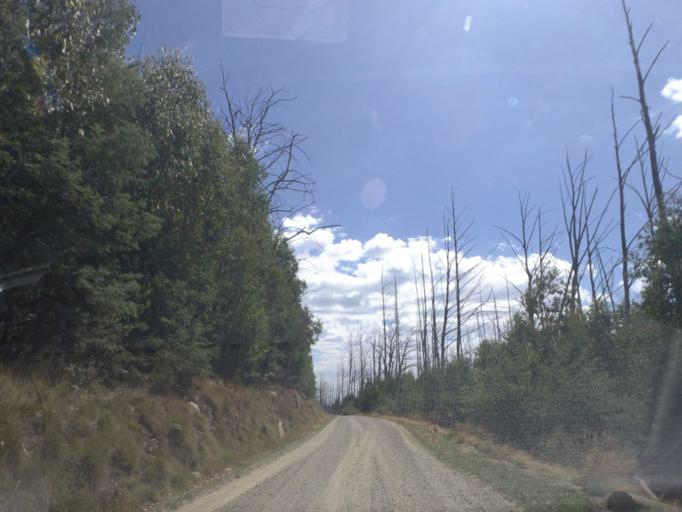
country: AU
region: Victoria
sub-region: Murrindindi
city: Alexandra
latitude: -37.4528
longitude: 145.7999
